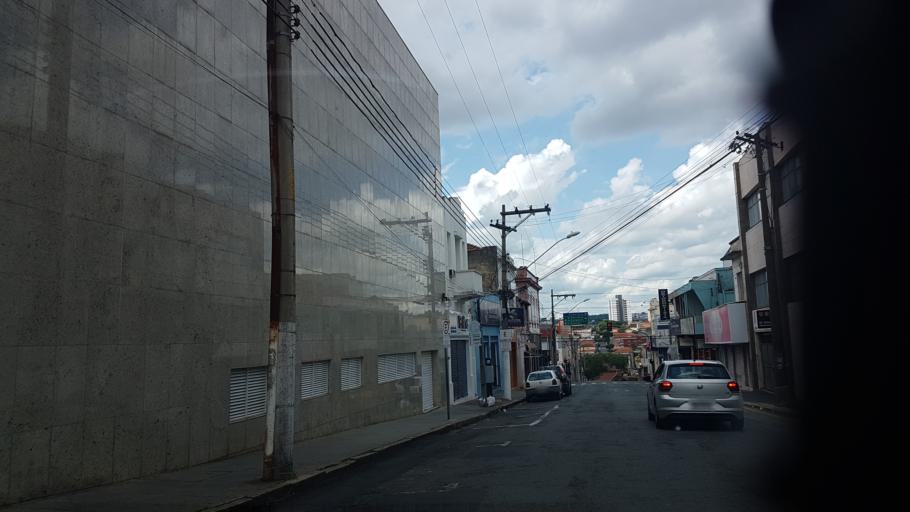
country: BR
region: Sao Paulo
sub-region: Limeira
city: Limeira
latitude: -22.5639
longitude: -47.4008
